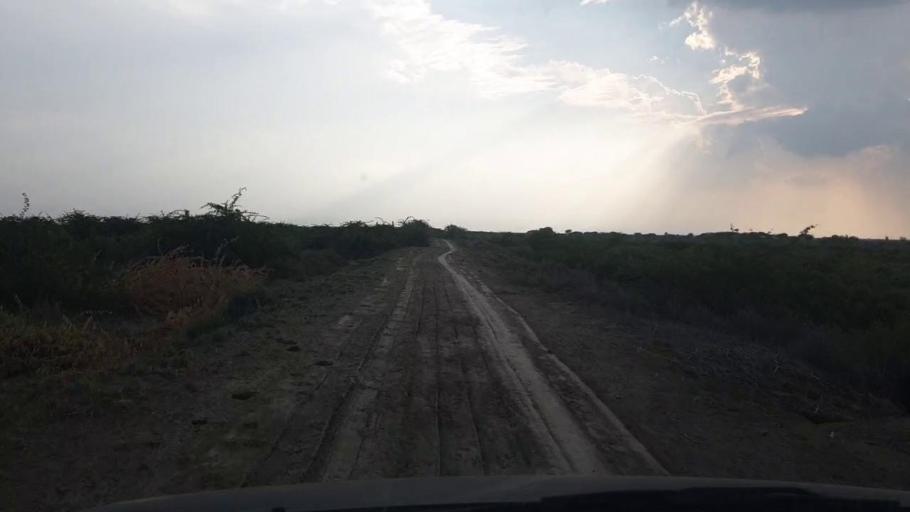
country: PK
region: Sindh
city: Badin
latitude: 24.4696
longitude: 68.6959
